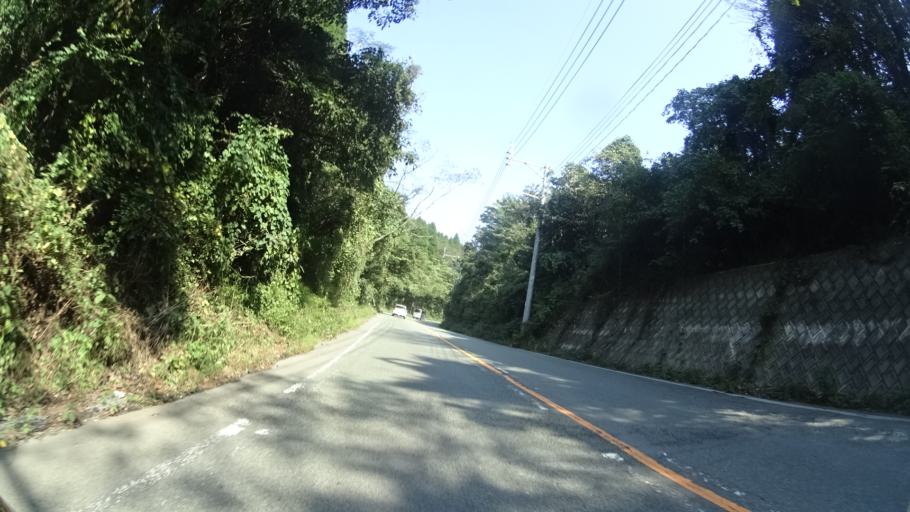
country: JP
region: Kumamoto
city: Ozu
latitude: 32.9106
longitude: 130.9549
